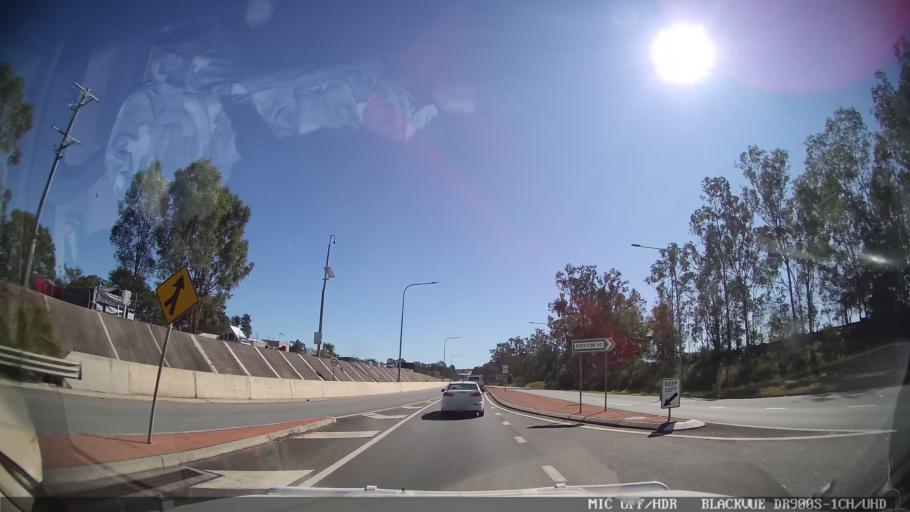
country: AU
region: Queensland
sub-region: Gympie Regional Council
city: Monkland
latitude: -26.2377
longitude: 152.6993
